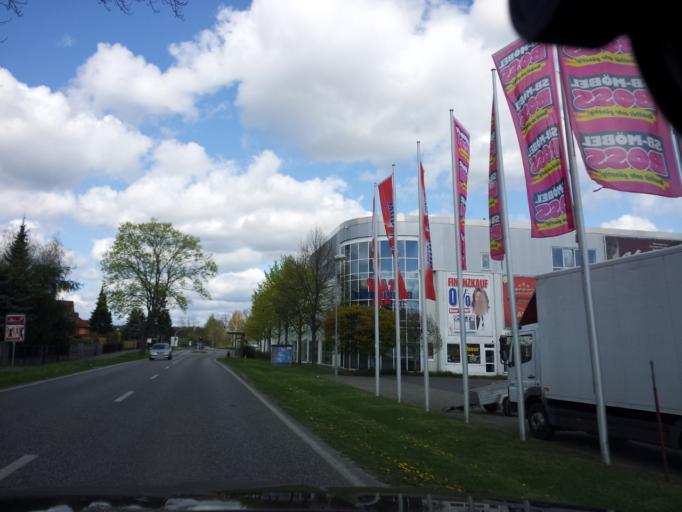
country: DE
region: Brandenburg
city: Bernau bei Berlin
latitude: 52.6847
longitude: 13.5982
